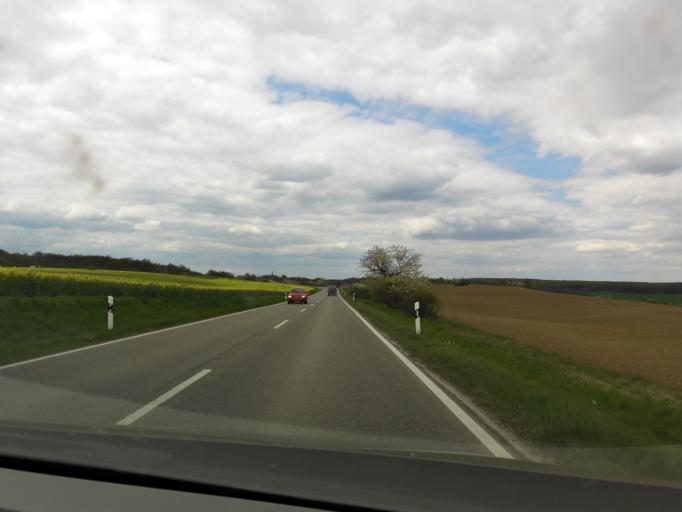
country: DE
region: Saxony-Anhalt
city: Eckartsberga
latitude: 51.1183
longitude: 11.5848
